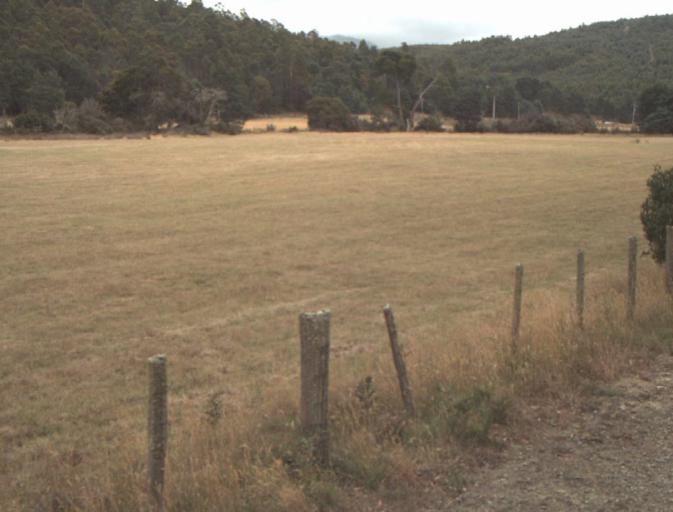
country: AU
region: Tasmania
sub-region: Northern Midlands
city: Evandale
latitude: -41.4647
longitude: 147.4955
